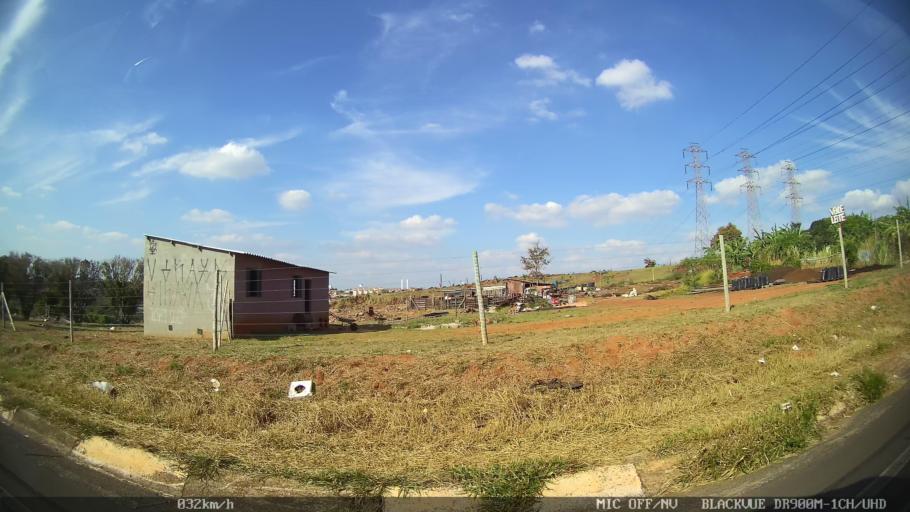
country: BR
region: Sao Paulo
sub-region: Hortolandia
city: Hortolandia
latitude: -22.8421
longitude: -47.2070
